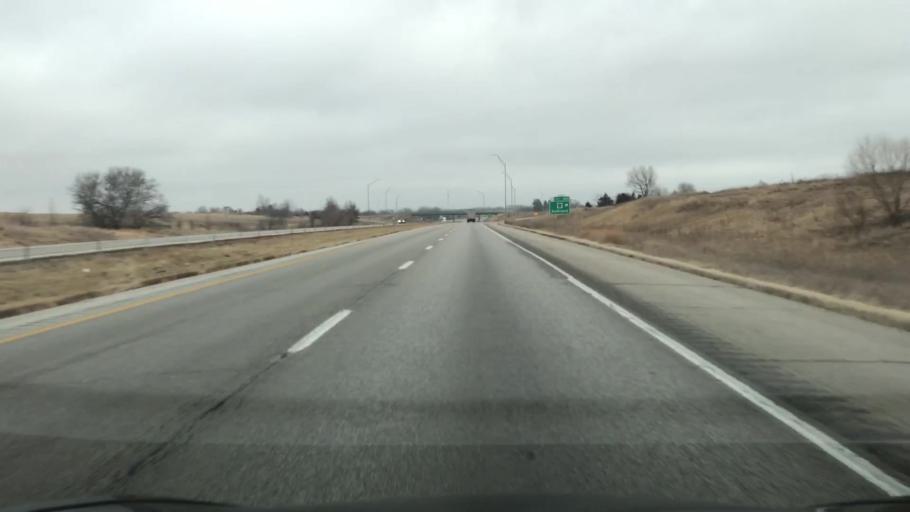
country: US
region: Iowa
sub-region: Madison County
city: Earlham
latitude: 41.5093
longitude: -94.2015
